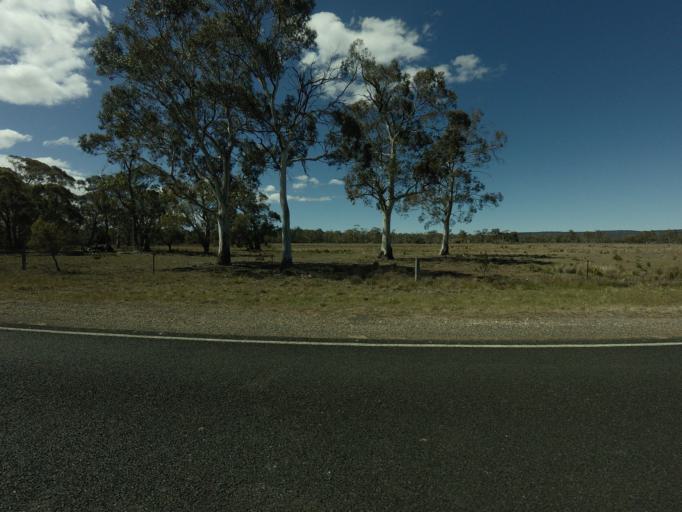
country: AU
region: Tasmania
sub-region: Break O'Day
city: St Helens
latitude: -42.0399
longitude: 148.0295
